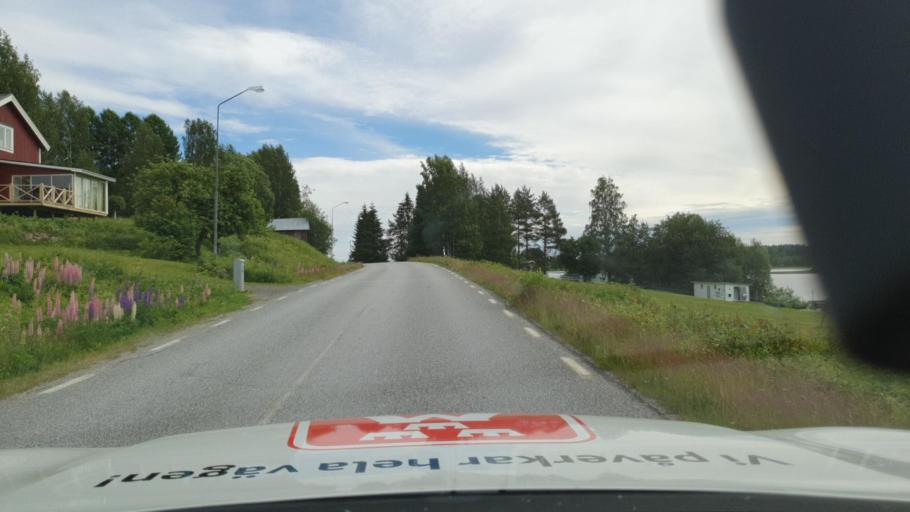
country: SE
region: Vaesterbotten
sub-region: Skelleftea Kommun
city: Burea
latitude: 64.4954
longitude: 21.0207
